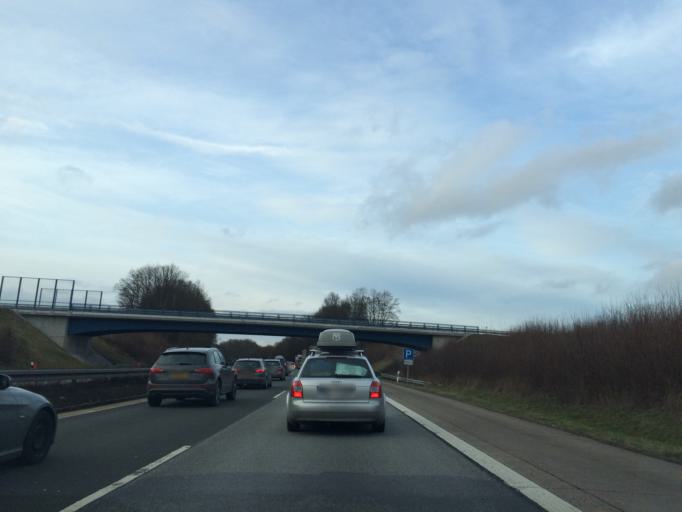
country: DE
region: Bavaria
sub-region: Regierungsbezirk Unterfranken
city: Marktheidenfeld
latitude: 49.8023
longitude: 9.5874
